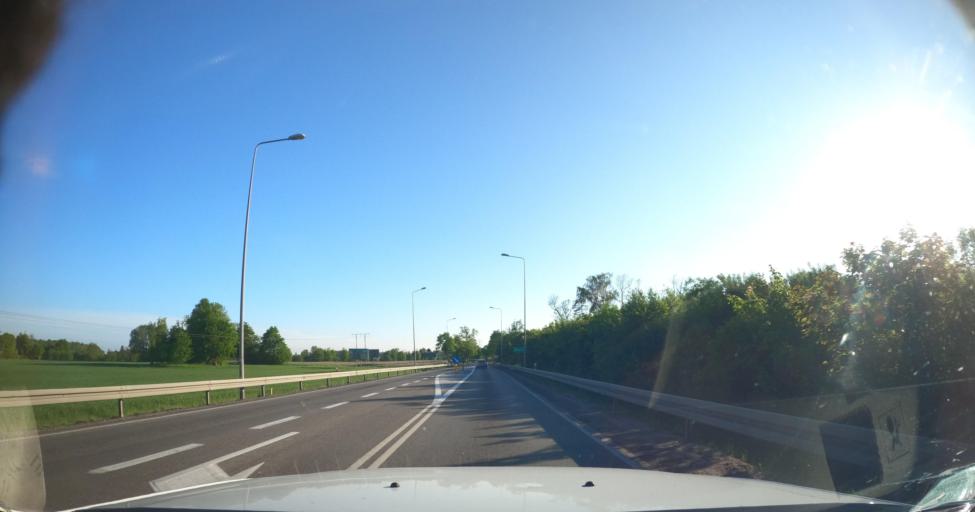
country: PL
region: Pomeranian Voivodeship
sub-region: Powiat kartuski
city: Banino
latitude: 54.3442
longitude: 18.4522
